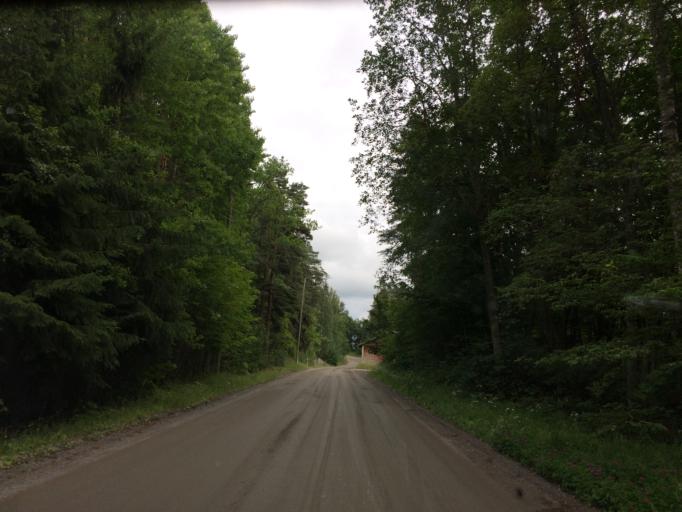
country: FI
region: Haeme
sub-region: Haemeenlinna
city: Haemeenlinna
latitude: 60.9693
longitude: 24.5210
